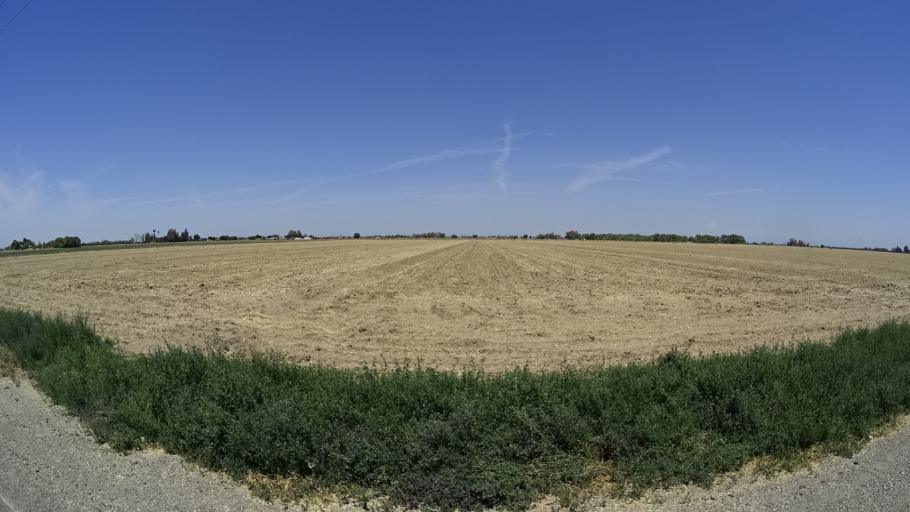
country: US
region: California
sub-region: Kings County
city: Lemoore
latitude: 36.2402
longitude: -119.7569
